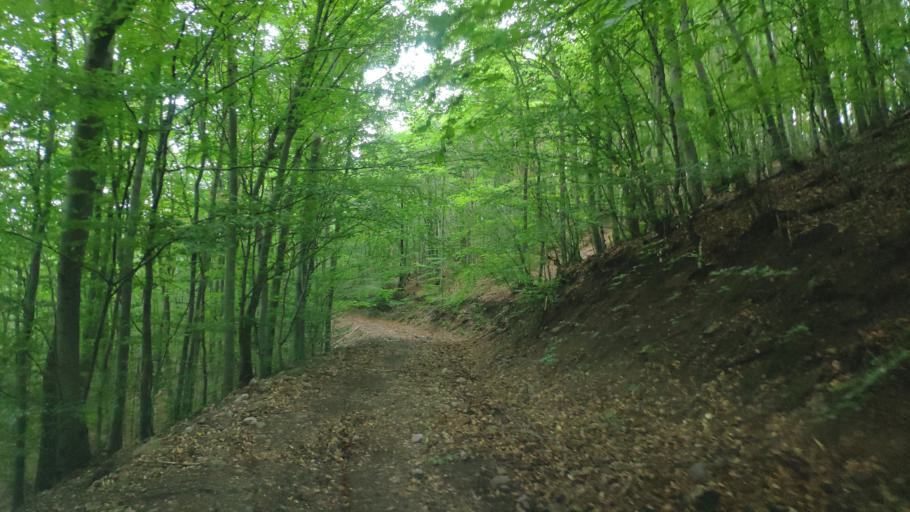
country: SK
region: Presovsky
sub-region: Okres Presov
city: Presov
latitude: 48.8677
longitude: 21.2239
